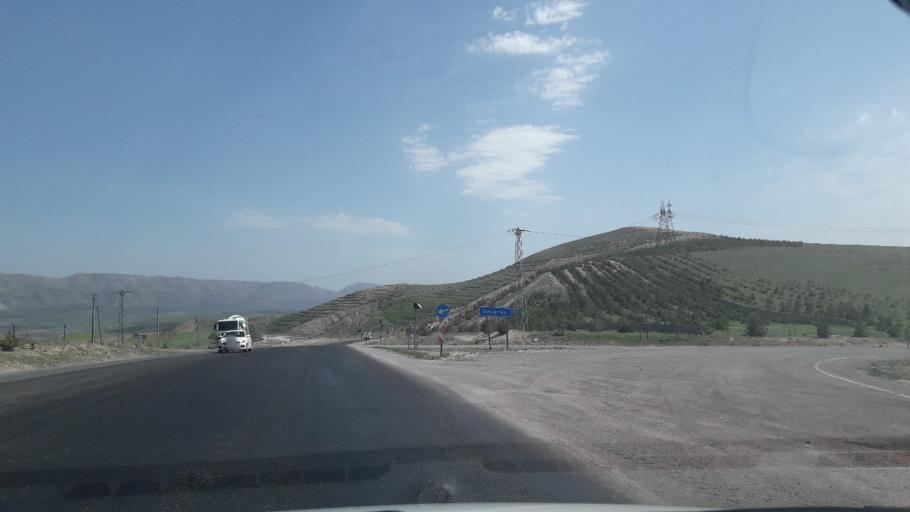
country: TR
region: Sivas
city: Deliktas
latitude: 39.3224
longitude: 37.1427
